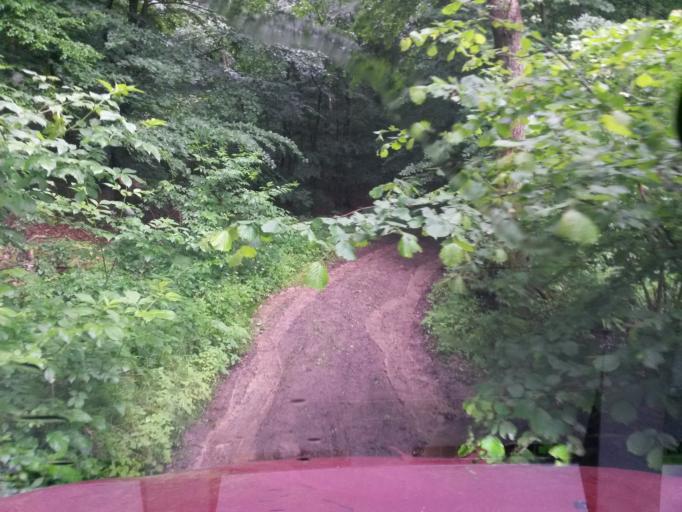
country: SK
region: Kosicky
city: Kosice
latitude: 48.7206
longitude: 21.1679
